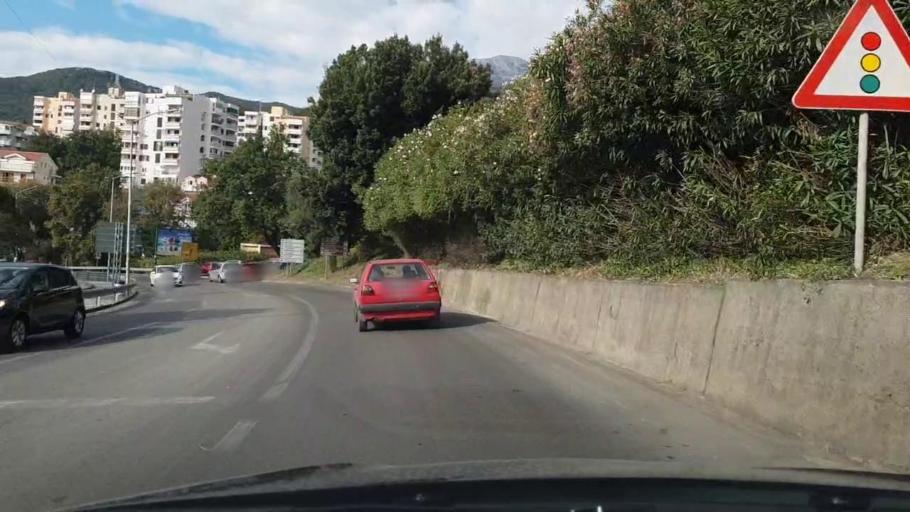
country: ME
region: Herceg Novi
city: Herceg-Novi
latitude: 42.4579
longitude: 18.5272
